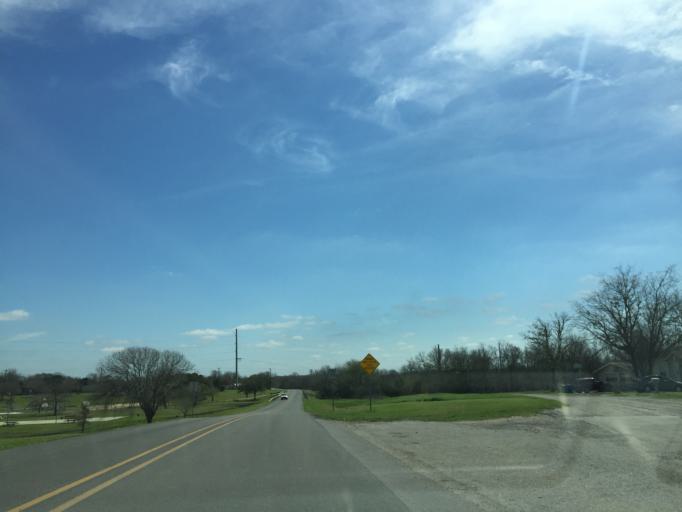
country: US
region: Texas
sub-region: Williamson County
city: Taylor
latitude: 30.5654
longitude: -97.4009
